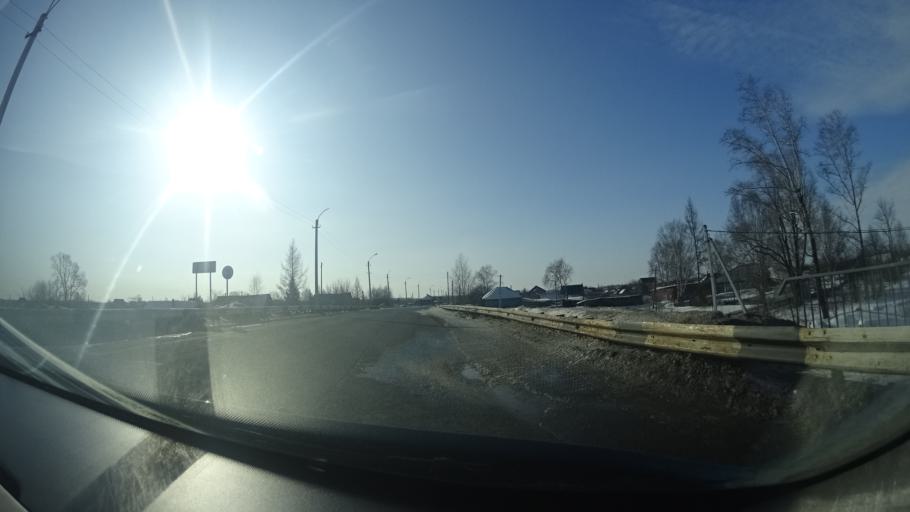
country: RU
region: Perm
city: Kuyeda
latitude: 56.4569
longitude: 55.5997
